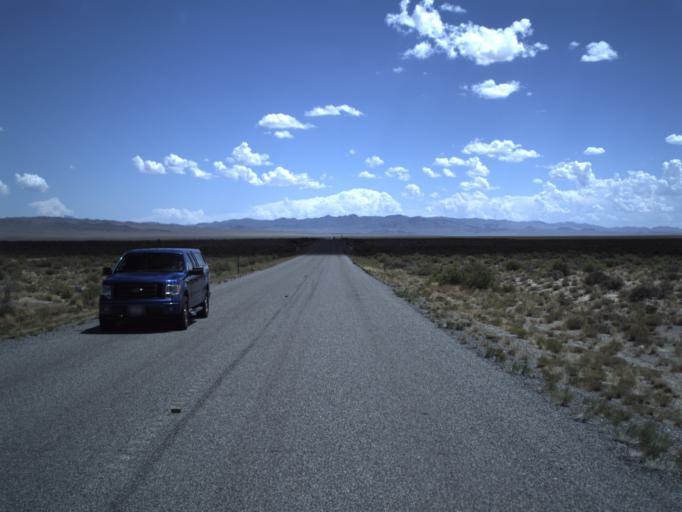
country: US
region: Nevada
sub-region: White Pine County
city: McGill
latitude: 39.0543
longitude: -114.0114
